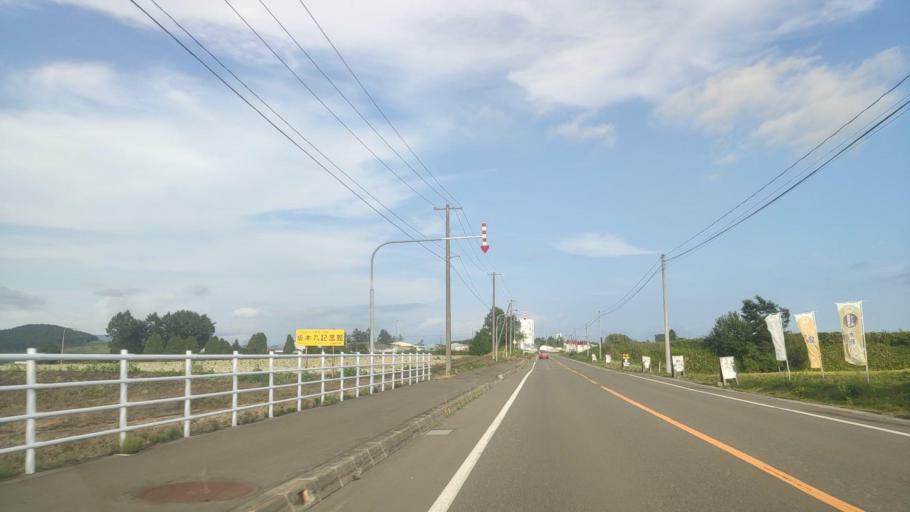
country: JP
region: Hokkaido
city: Iwamizawa
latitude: 43.0269
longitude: 141.8355
